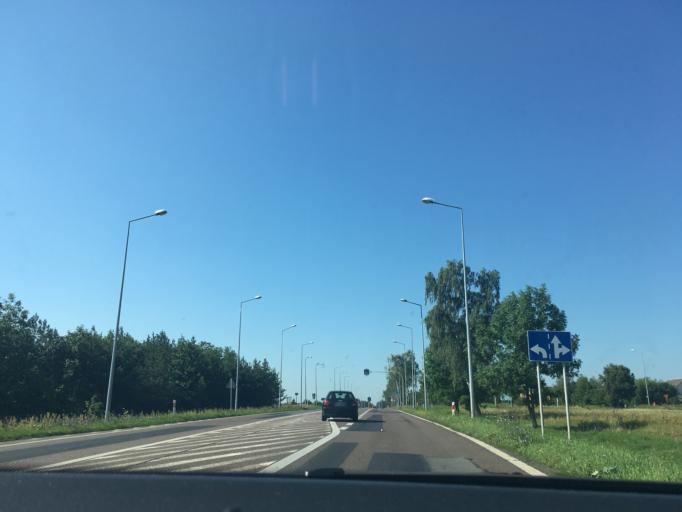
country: PL
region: Lublin Voivodeship
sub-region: Powiat radzynski
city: Borki
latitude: 51.7185
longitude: 22.5285
